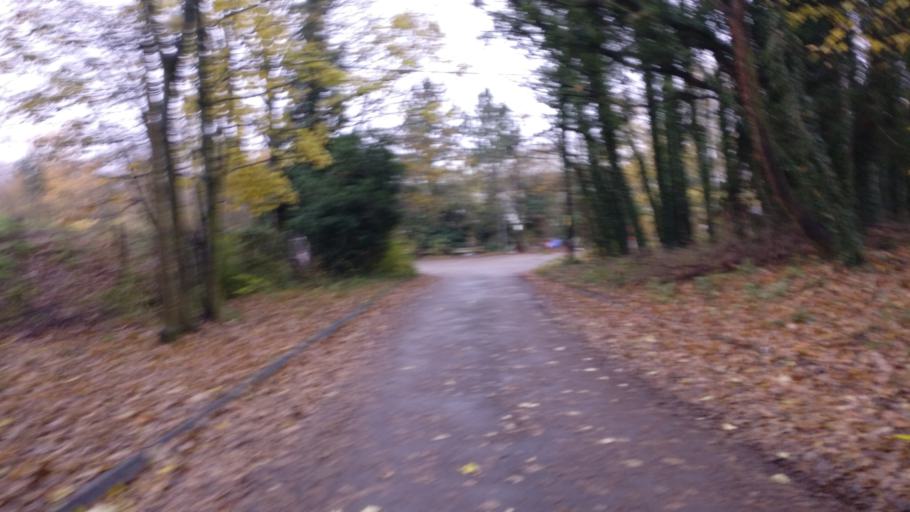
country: GB
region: England
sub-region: Hampshire
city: Basingstoke
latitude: 51.2667
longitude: -1.1053
